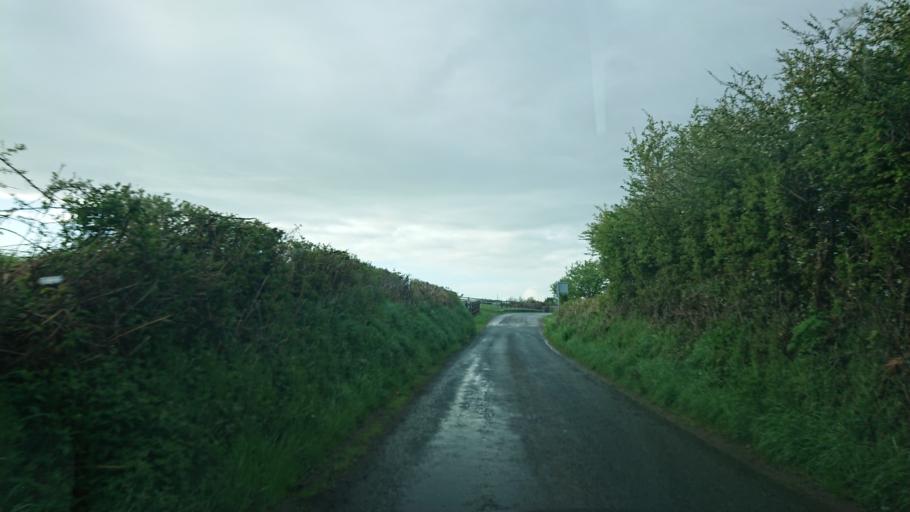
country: IE
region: Munster
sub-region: Waterford
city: Waterford
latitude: 52.2235
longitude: -7.1318
